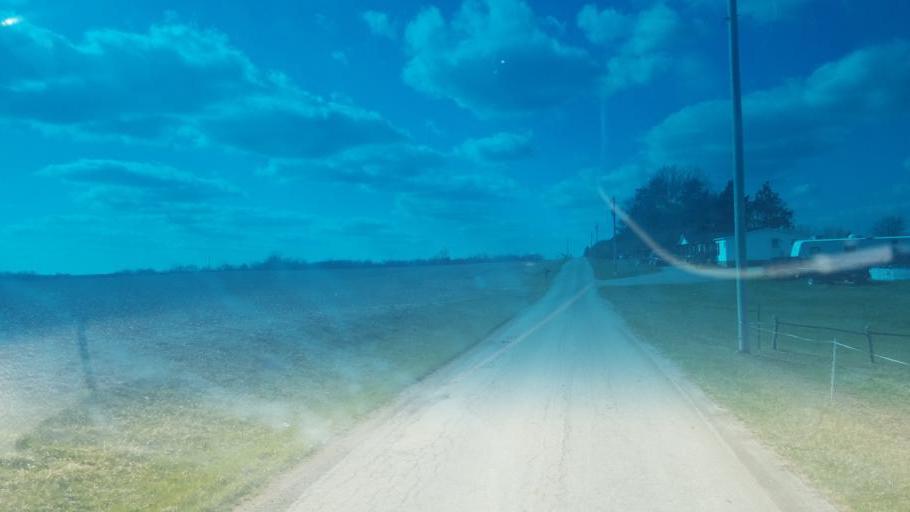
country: US
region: Ohio
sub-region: Highland County
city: Greenfield
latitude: 39.3003
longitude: -83.4397
